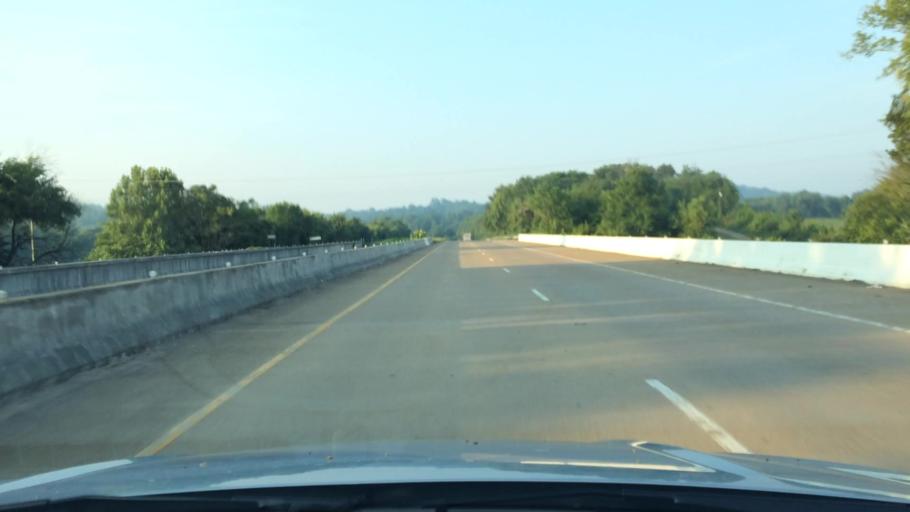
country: US
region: Tennessee
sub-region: Giles County
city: Pulaski
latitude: 35.1952
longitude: -87.0641
